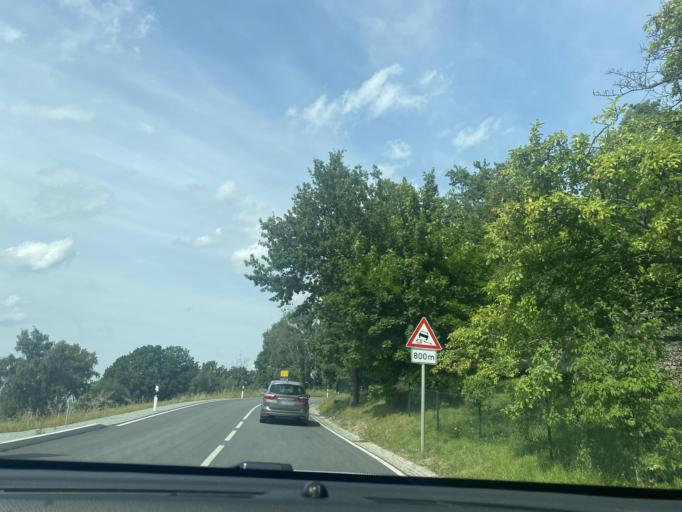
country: DE
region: Saxony
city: Herrnhut
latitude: 50.9641
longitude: 14.7382
